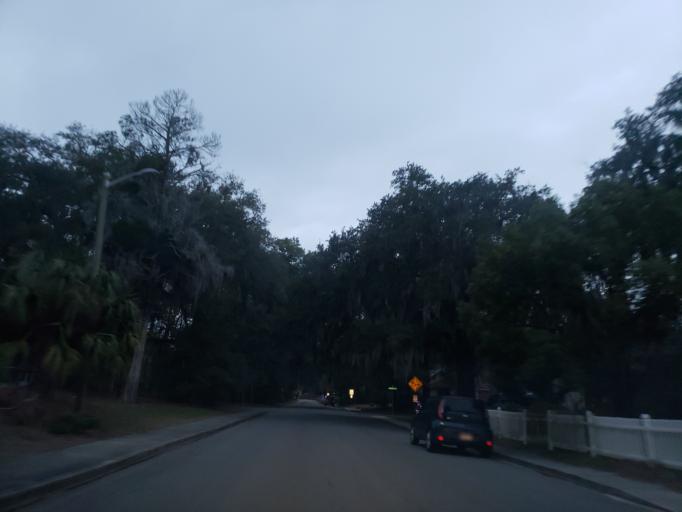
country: US
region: Georgia
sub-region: Chatham County
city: Thunderbolt
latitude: 32.0570
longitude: -81.0656
